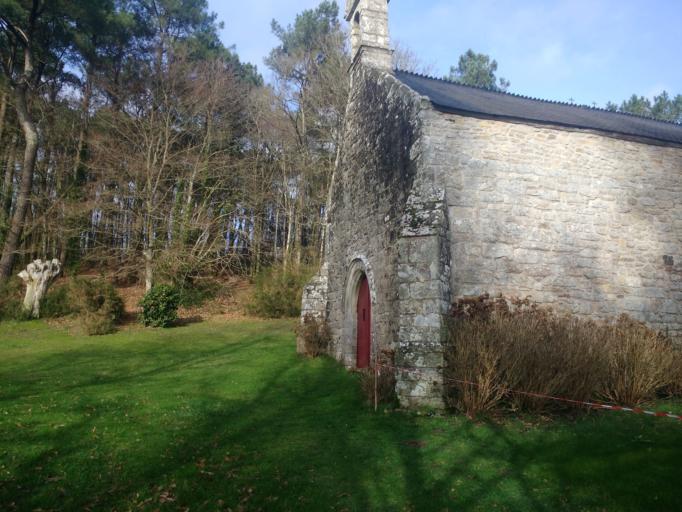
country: FR
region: Brittany
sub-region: Departement du Morbihan
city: Limerzel
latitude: 47.6537
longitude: -2.3554
